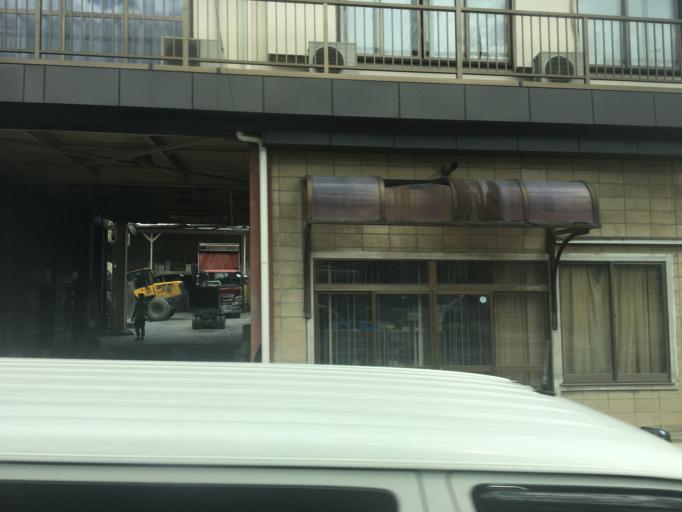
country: JP
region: Tokyo
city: Higashimurayama-shi
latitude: 35.7633
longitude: 139.4935
